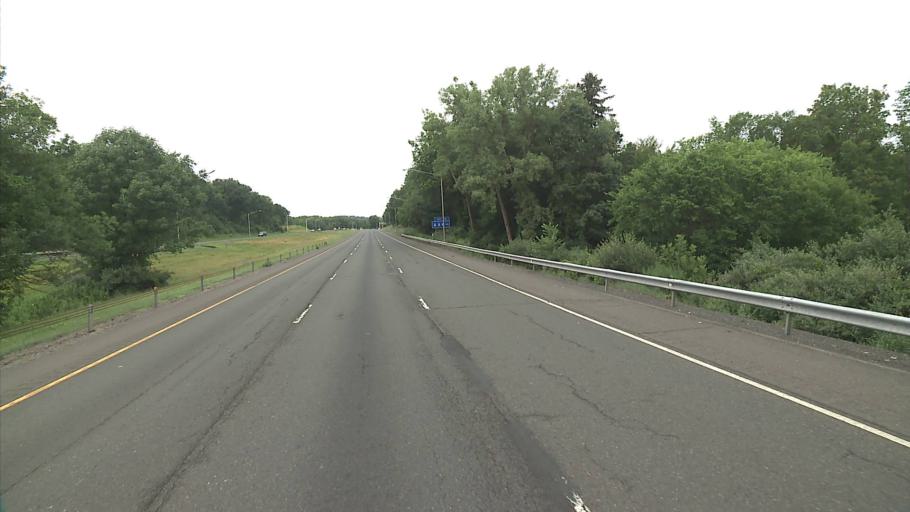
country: US
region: Connecticut
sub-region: Fairfield County
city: Newtown
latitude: 41.4164
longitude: -73.2834
